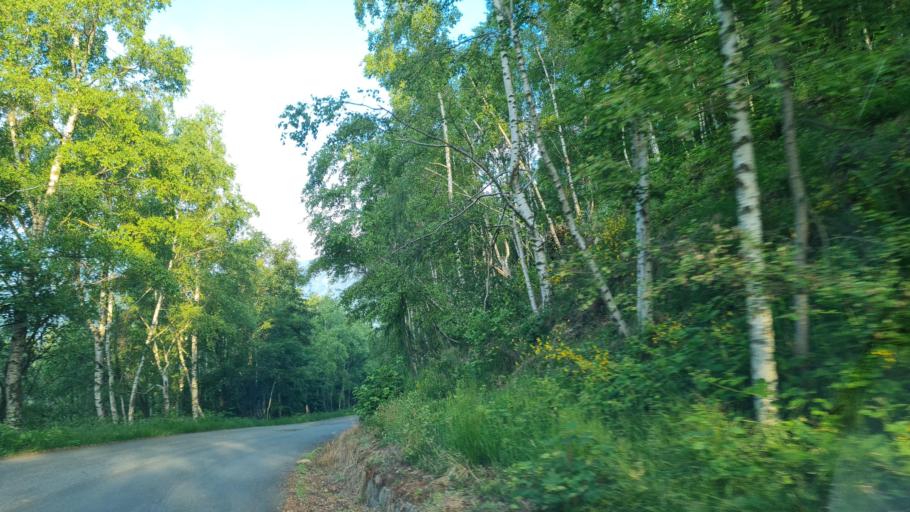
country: IT
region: Piedmont
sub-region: Provincia di Biella
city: Sordevolo
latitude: 45.5896
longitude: 7.9723
